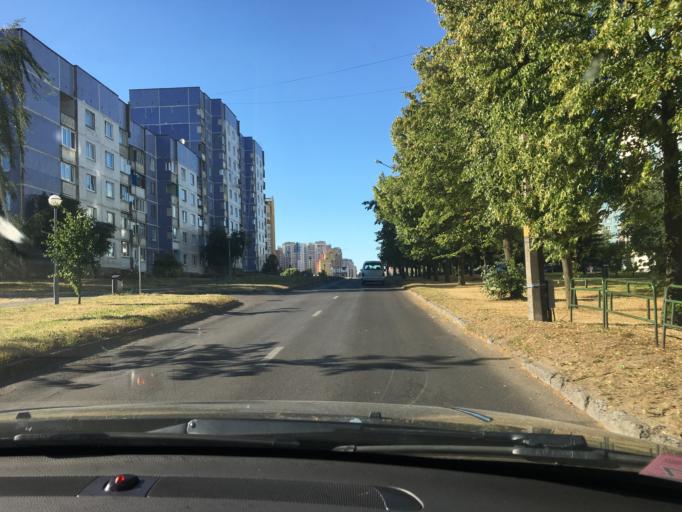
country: BY
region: Grodnenskaya
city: Hrodna
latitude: 53.7042
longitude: 23.8496
